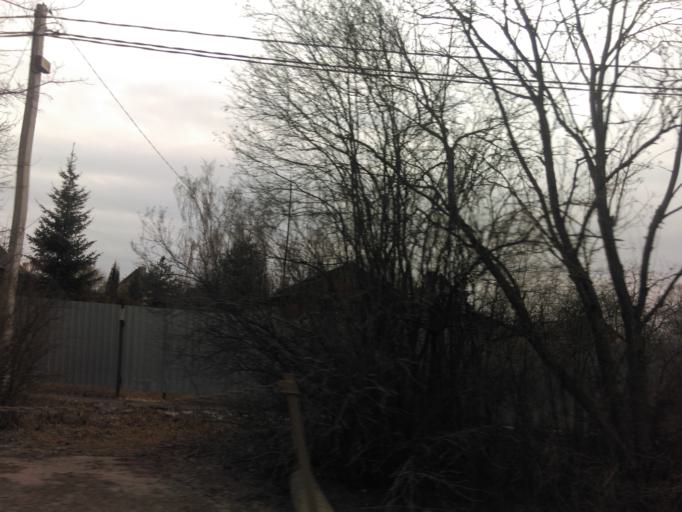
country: RU
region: Moskovskaya
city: Gorki Vtoryye
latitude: 55.7152
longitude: 37.1033
